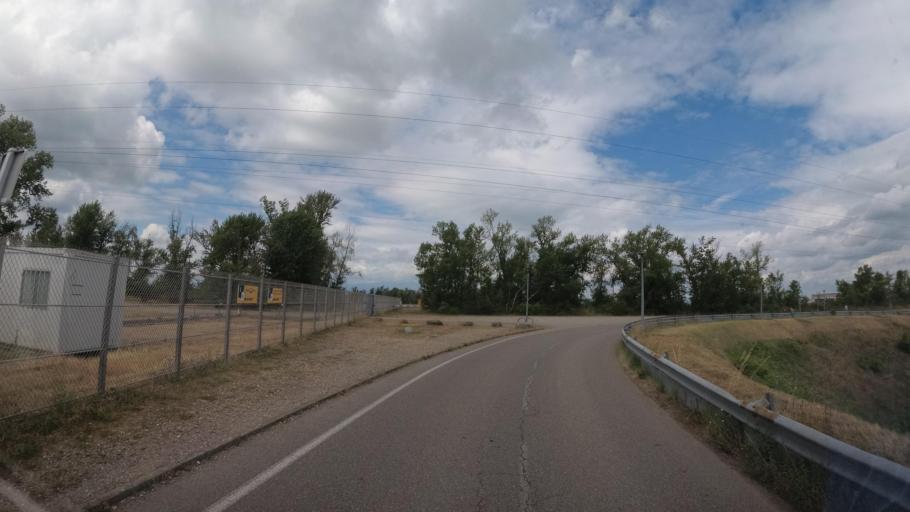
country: FR
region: Alsace
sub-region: Departement du Haut-Rhin
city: Fessenheim
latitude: 47.9116
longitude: 7.5714
